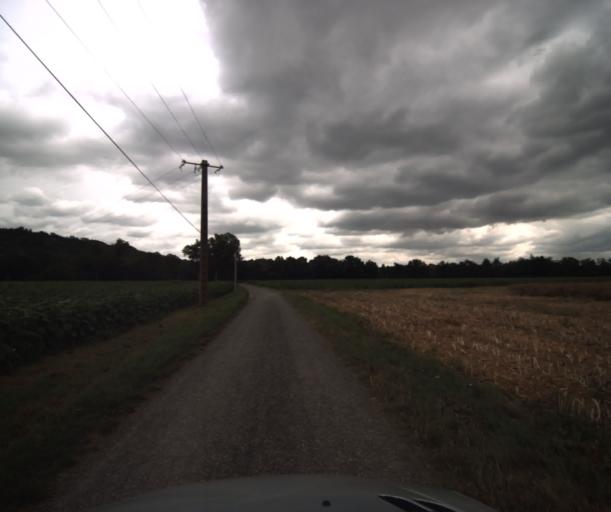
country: FR
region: Midi-Pyrenees
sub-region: Departement de la Haute-Garonne
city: Labarthe-sur-Leze
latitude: 43.4639
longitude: 1.4155
